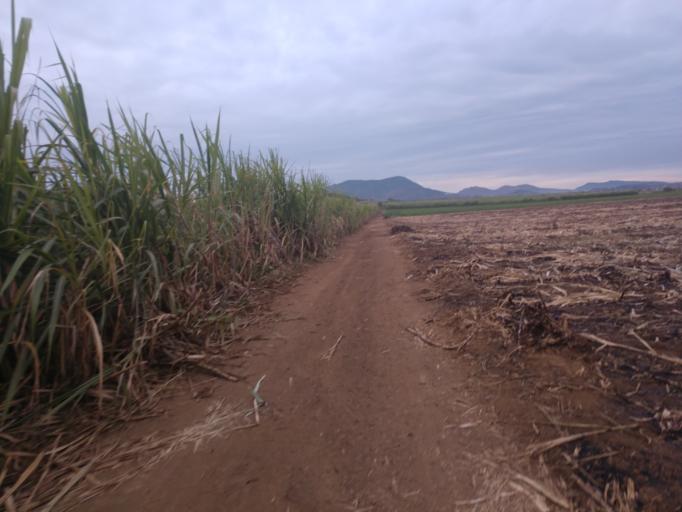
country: MX
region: Nayarit
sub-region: Tepic
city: La Corregidora
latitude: 21.4758
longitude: -104.8080
